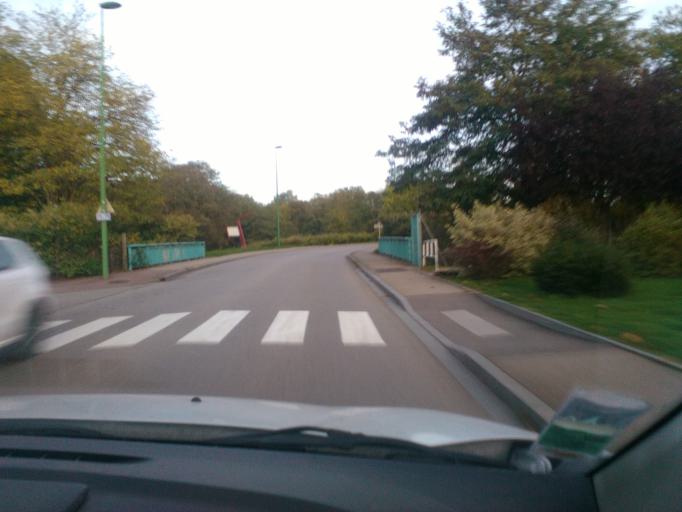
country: FR
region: Lorraine
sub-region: Departement des Vosges
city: Golbey
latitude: 48.1939
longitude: 6.4481
